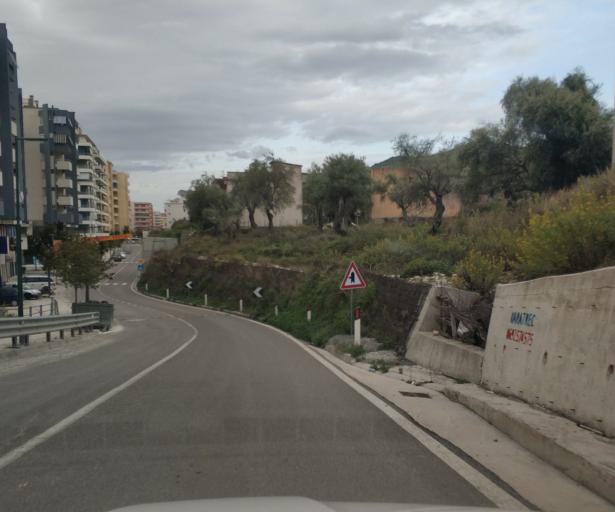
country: AL
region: Vlore
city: Vlore
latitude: 40.4352
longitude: 19.4964
